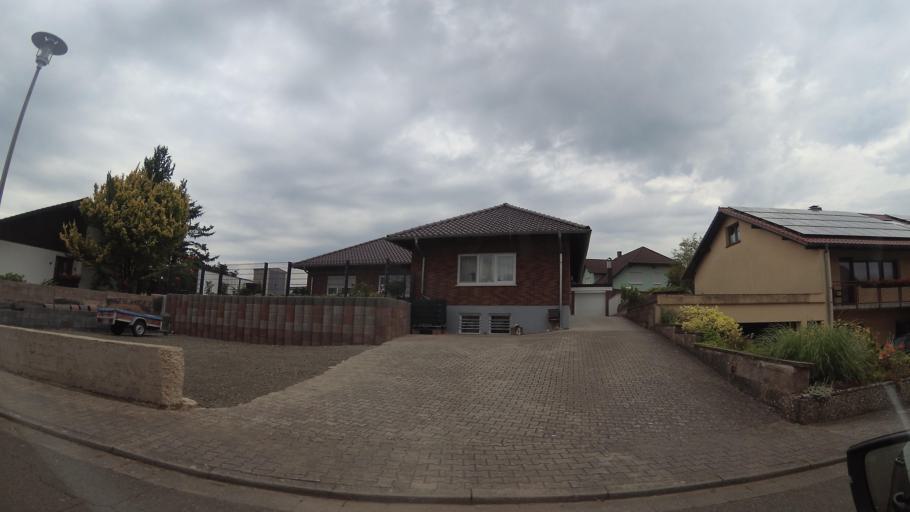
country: DE
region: Rheinland-Pfalz
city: Hutschenhausen
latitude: 49.4193
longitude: 7.4676
